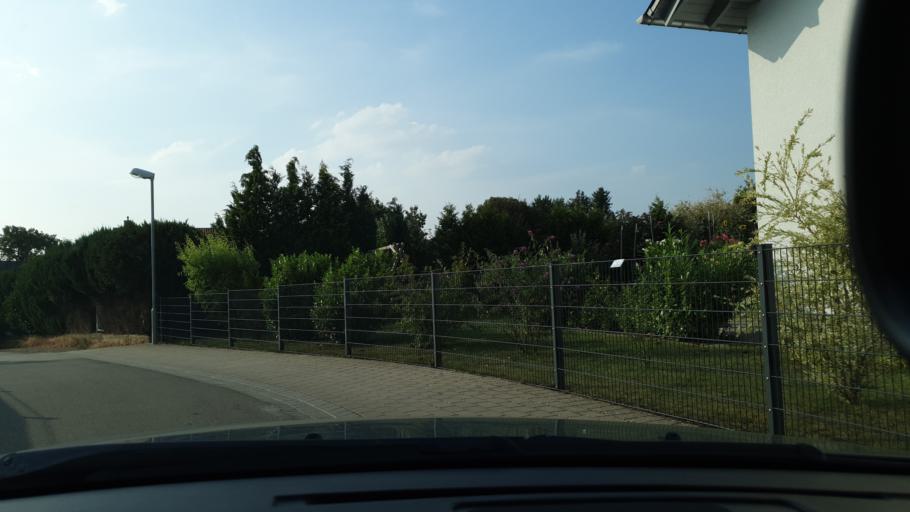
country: DE
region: Rheinland-Pfalz
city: Katzweiler
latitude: 49.4703
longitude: 7.6940
